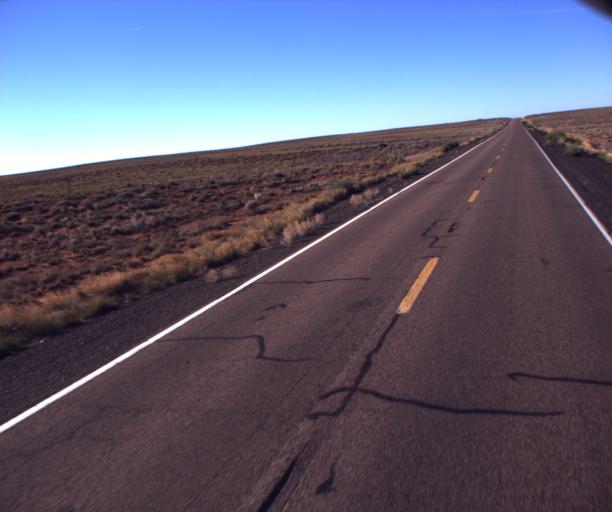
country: US
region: Arizona
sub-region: Navajo County
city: Holbrook
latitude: 34.8434
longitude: -110.1791
